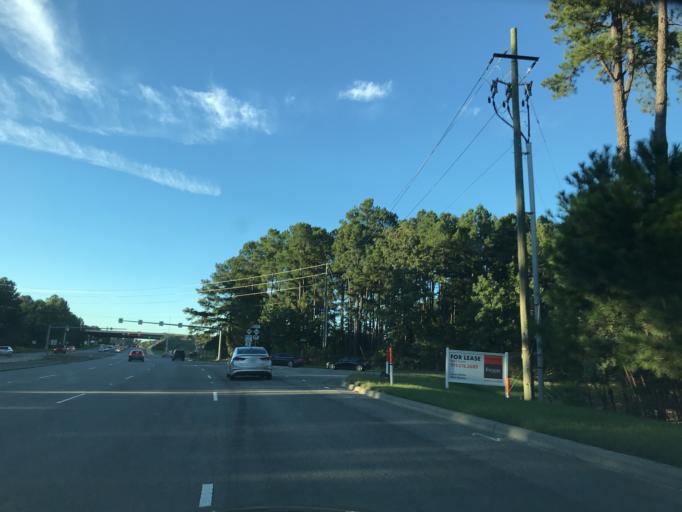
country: US
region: North Carolina
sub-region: Wake County
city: Morrisville
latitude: 35.8581
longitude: -78.8429
